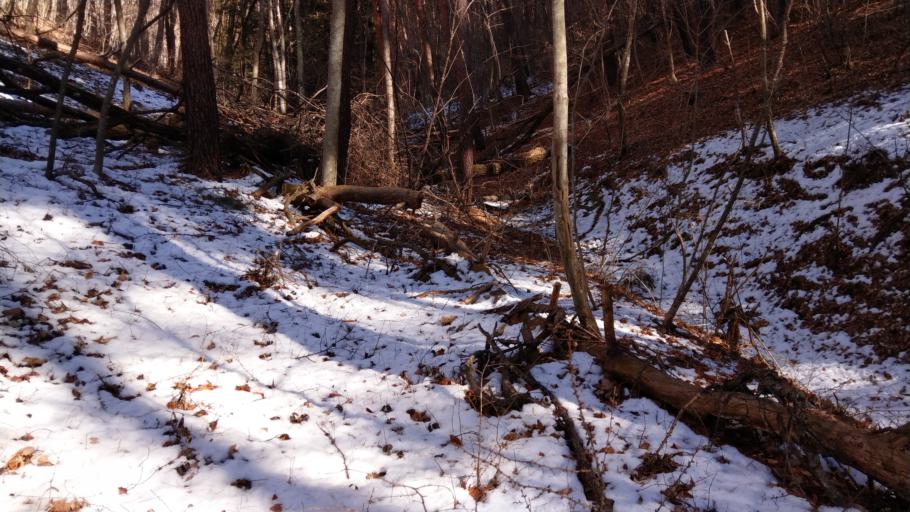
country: JP
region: Nagano
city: Komoro
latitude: 36.3651
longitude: 138.4321
